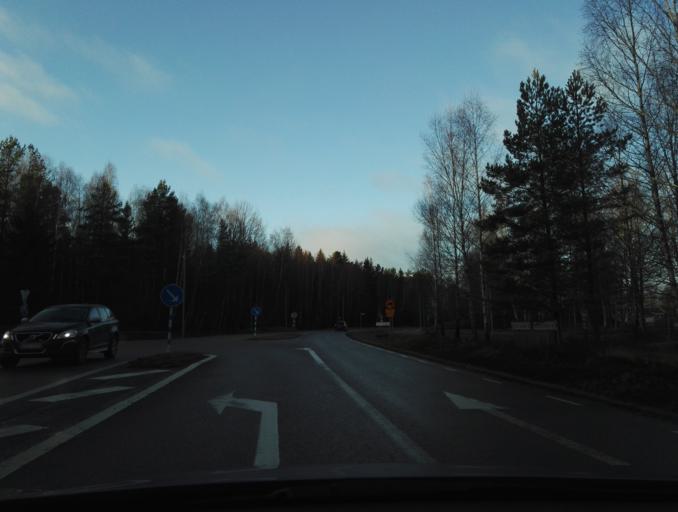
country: SE
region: Kronoberg
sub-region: Vaxjo Kommun
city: Vaexjoe
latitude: 56.9035
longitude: 14.7957
